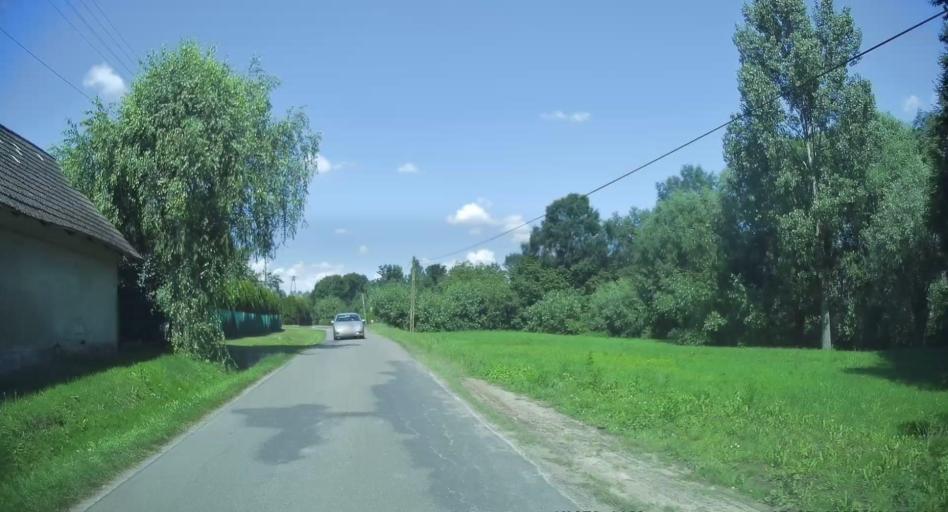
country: PL
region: Subcarpathian Voivodeship
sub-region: Powiat jaroslawski
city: Sosnica
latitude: 49.8635
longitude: 22.8771
